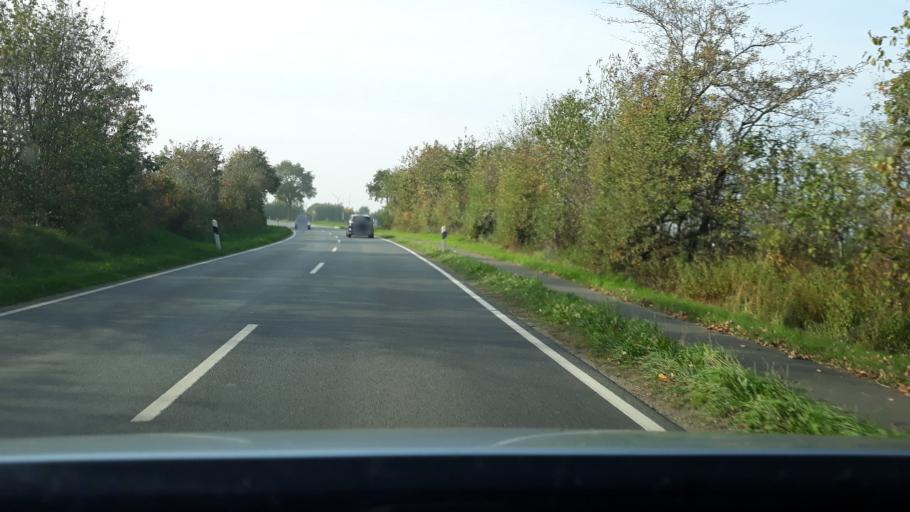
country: DE
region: Schleswig-Holstein
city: Owschlag
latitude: 54.4023
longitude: 9.6069
